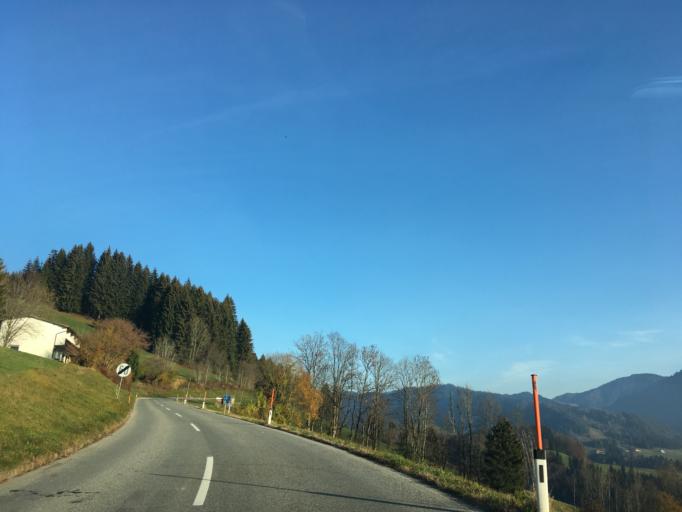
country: AT
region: Tyrol
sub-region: Politischer Bezirk Kufstein
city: Rettenschoss
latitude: 47.6580
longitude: 12.2446
